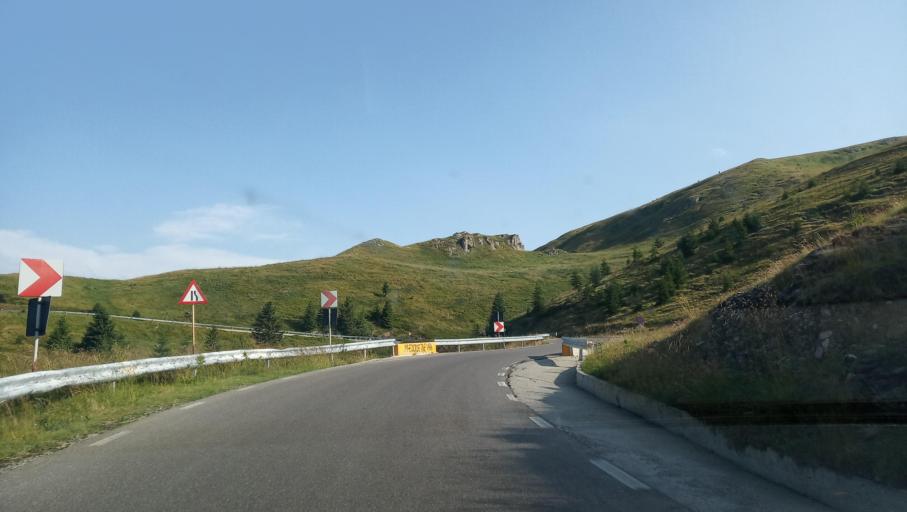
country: RO
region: Prahova
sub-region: Oras Sinaia
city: Sinaia
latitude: 45.3266
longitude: 25.4668
